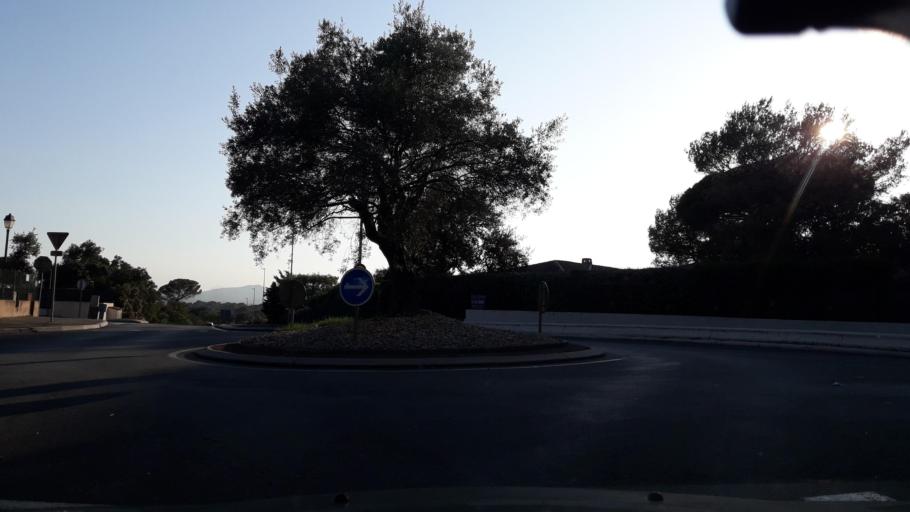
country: FR
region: Provence-Alpes-Cote d'Azur
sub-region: Departement du Var
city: Saint-Raphael
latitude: 43.4413
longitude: 6.7910
